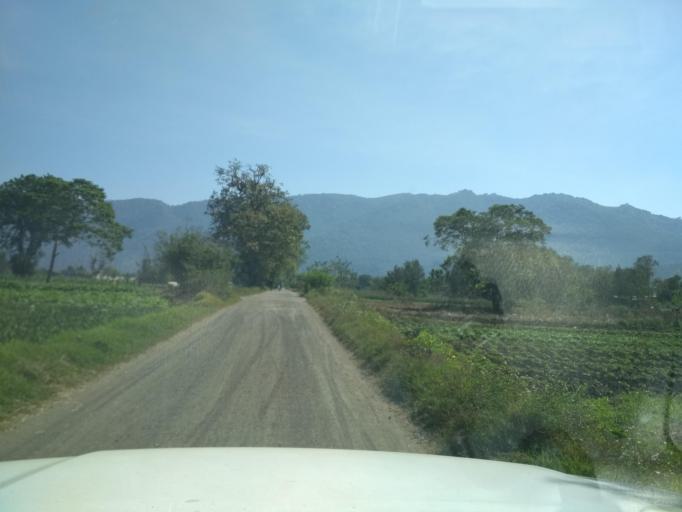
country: MX
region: Veracruz
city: Jalapilla
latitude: 18.8113
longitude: -97.0842
